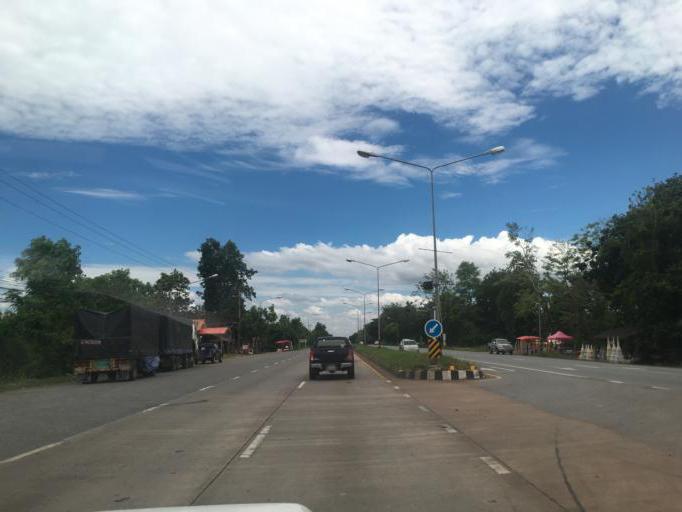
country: TH
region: Khon Kaen
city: Nam Phong
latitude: 16.6403
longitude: 102.8000
